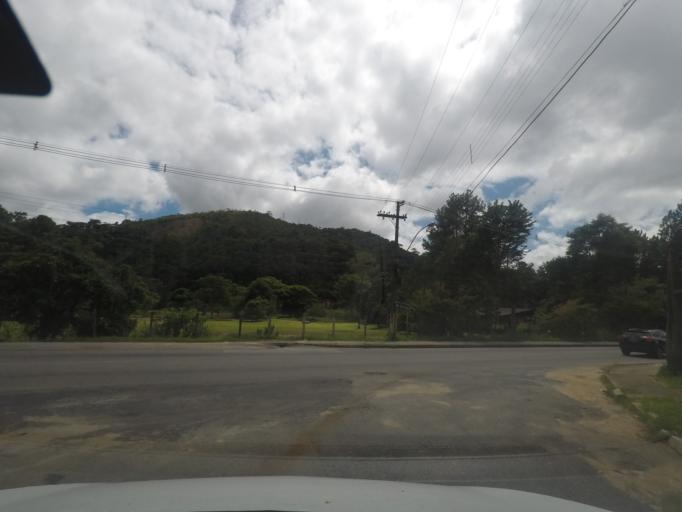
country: BR
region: Rio de Janeiro
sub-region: Teresopolis
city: Teresopolis
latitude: -22.3977
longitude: -42.9842
